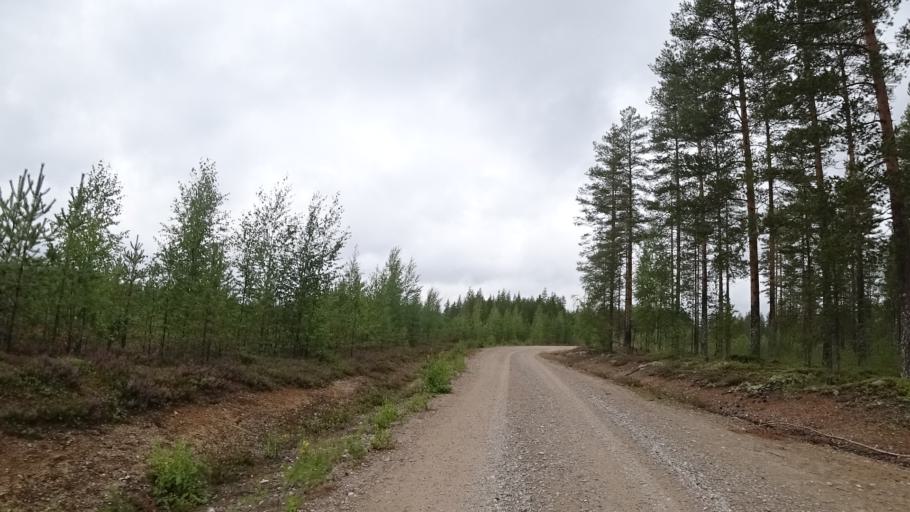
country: FI
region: North Karelia
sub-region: Pielisen Karjala
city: Lieksa
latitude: 63.5190
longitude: 30.1110
